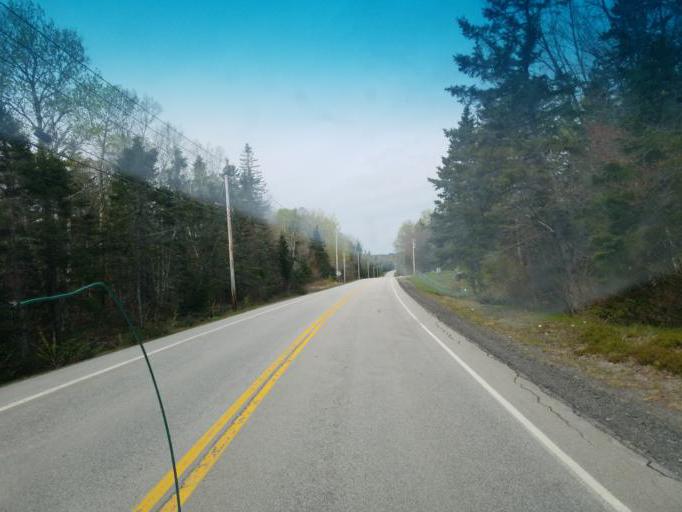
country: US
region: Maine
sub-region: Washington County
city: Eastport
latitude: 44.8009
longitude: -67.1253
